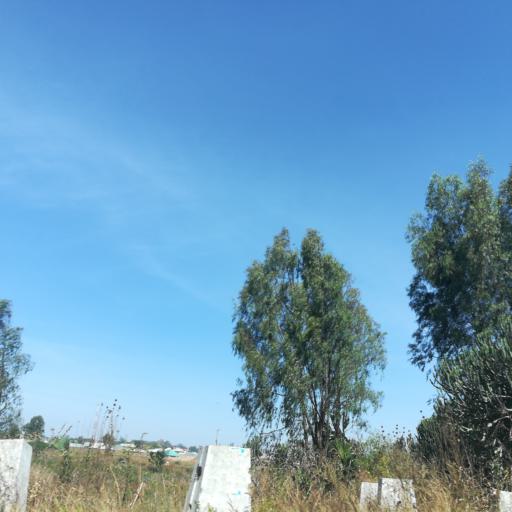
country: NG
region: Plateau
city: Bukuru
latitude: 9.7588
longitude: 8.8656
